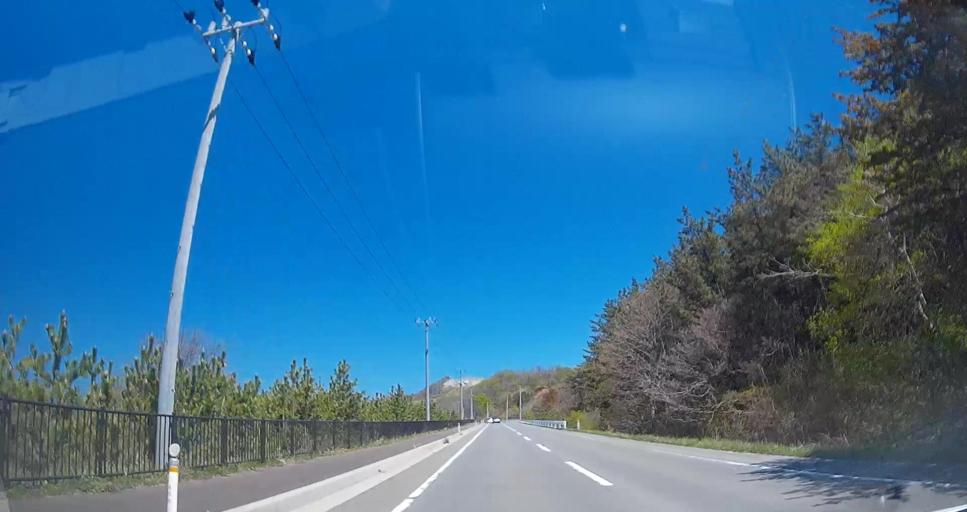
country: JP
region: Aomori
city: Mutsu
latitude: 41.3932
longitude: 141.4186
